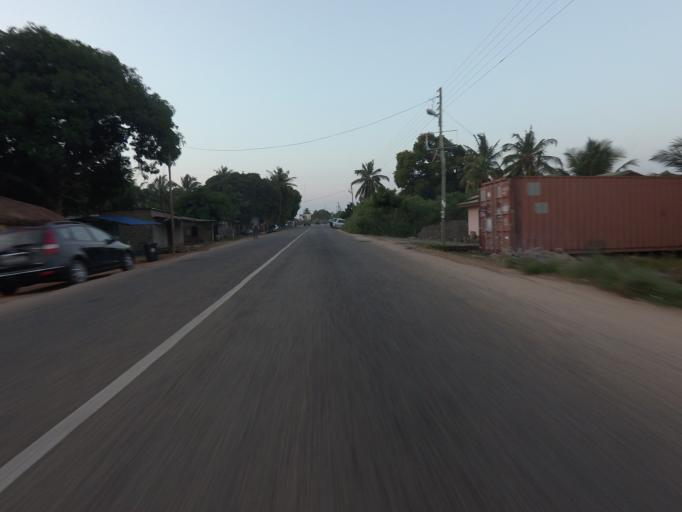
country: GH
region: Volta
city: Keta
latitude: 5.8747
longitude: 0.9804
